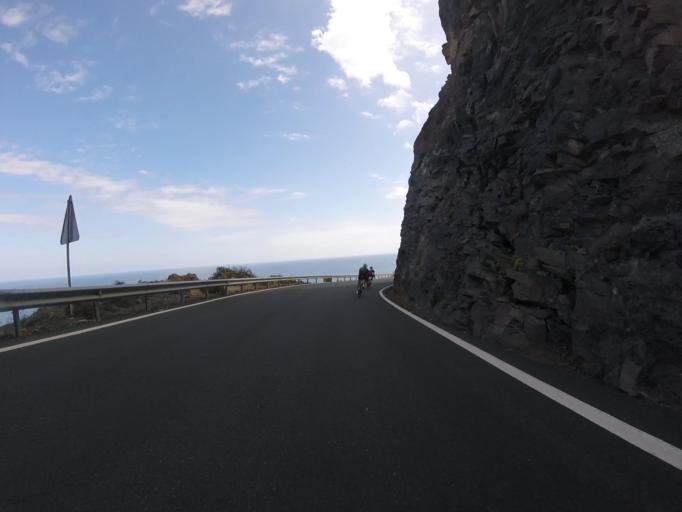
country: ES
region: Canary Islands
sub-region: Provincia de Las Palmas
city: Moya
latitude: 28.1421
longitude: -15.5921
